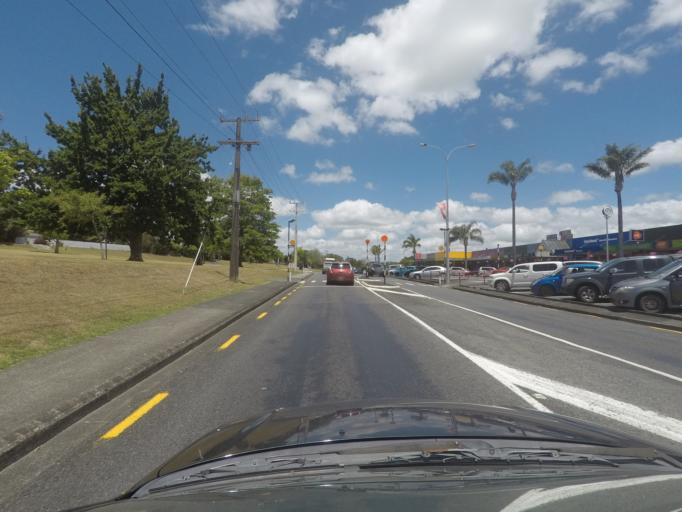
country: NZ
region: Northland
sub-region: Whangarei
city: Whangarei
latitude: -35.7546
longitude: 174.3685
